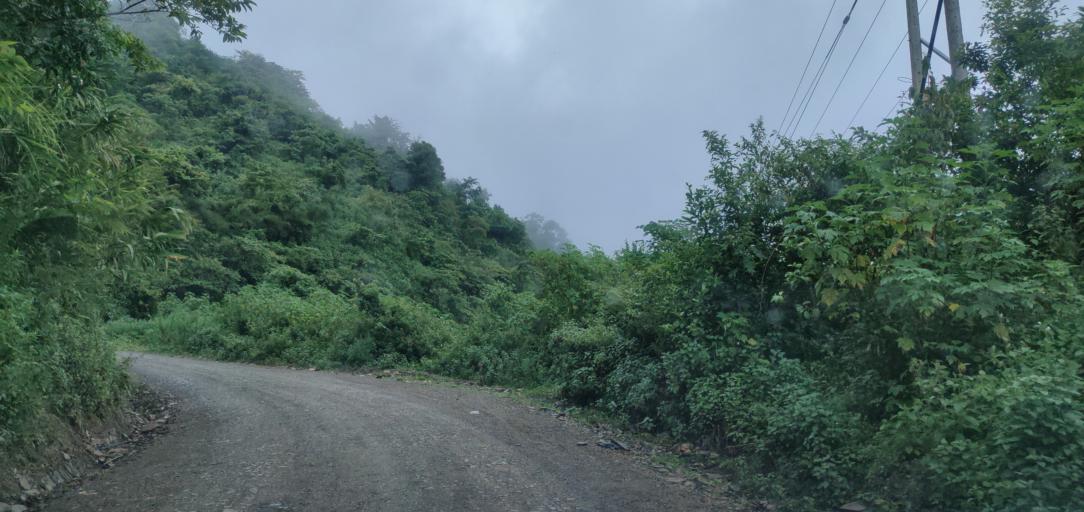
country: LA
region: Phongsali
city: Phongsali
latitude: 21.4507
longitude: 102.1625
